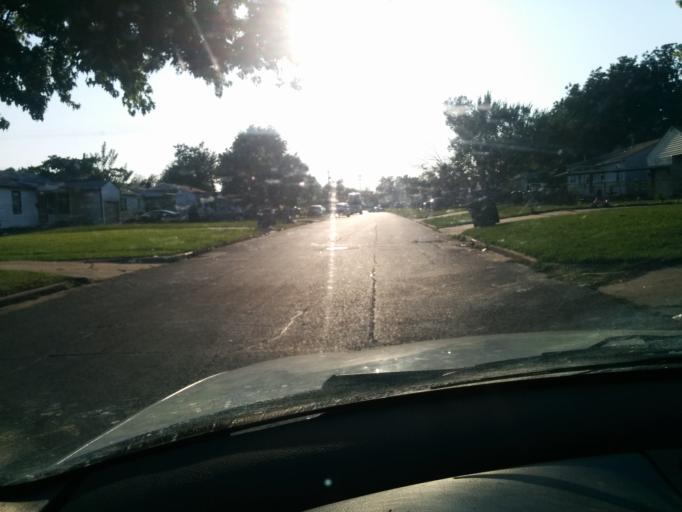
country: US
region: Oklahoma
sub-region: Tulsa County
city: Tulsa
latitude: 36.1686
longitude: -95.8963
